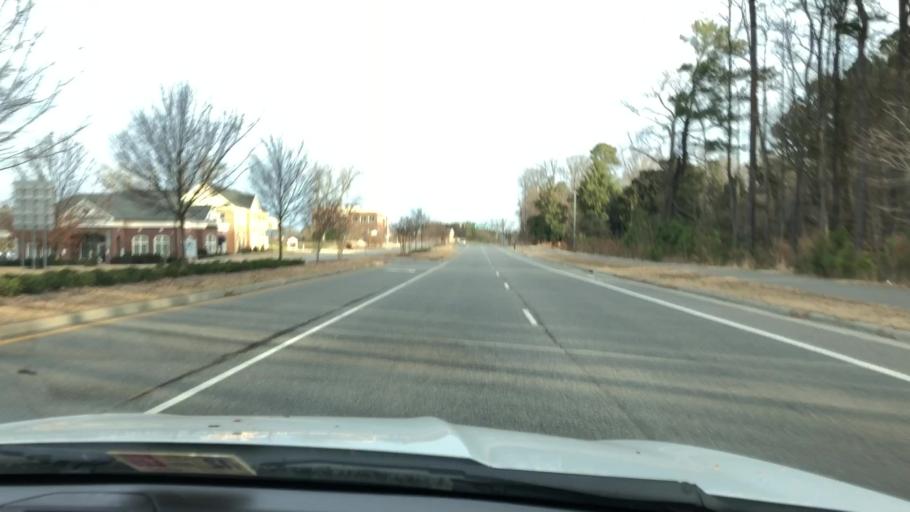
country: US
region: Virginia
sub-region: James City County
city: Williamsburg
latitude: 37.2772
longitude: -76.7382
